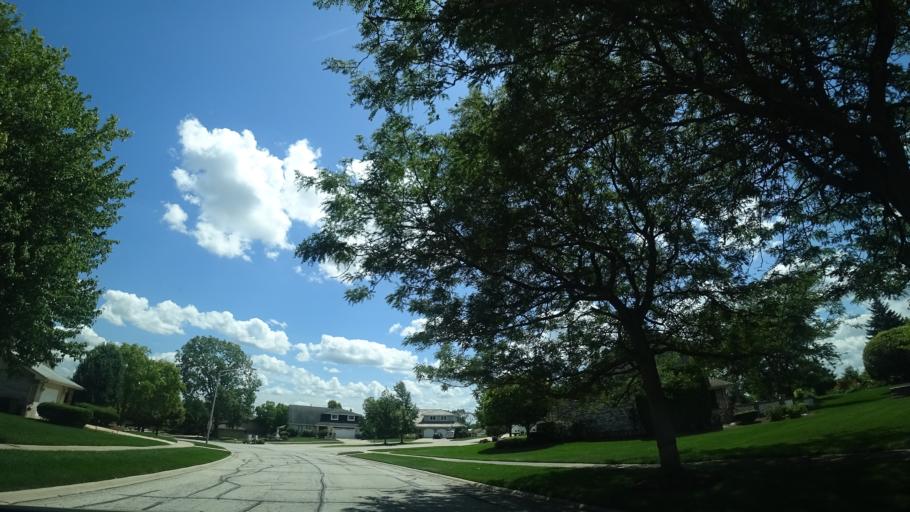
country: US
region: Illinois
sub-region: Will County
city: Homer Glen
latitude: 41.5772
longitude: -87.9024
